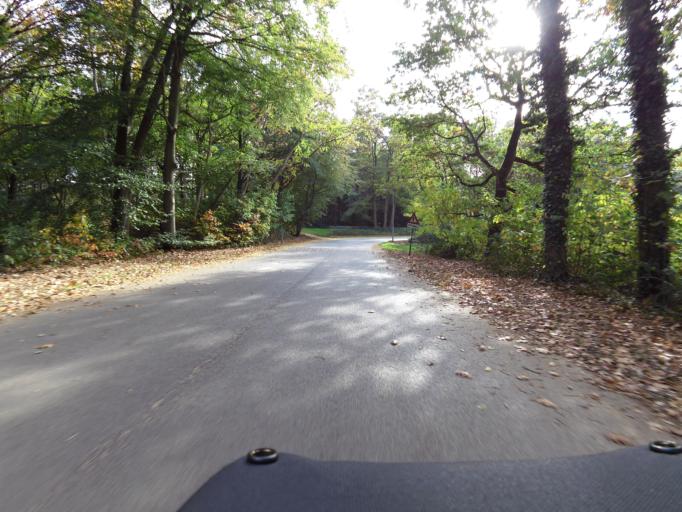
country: NL
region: Gelderland
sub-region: Gemeente Ede
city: Ede
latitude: 52.0321
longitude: 5.6758
